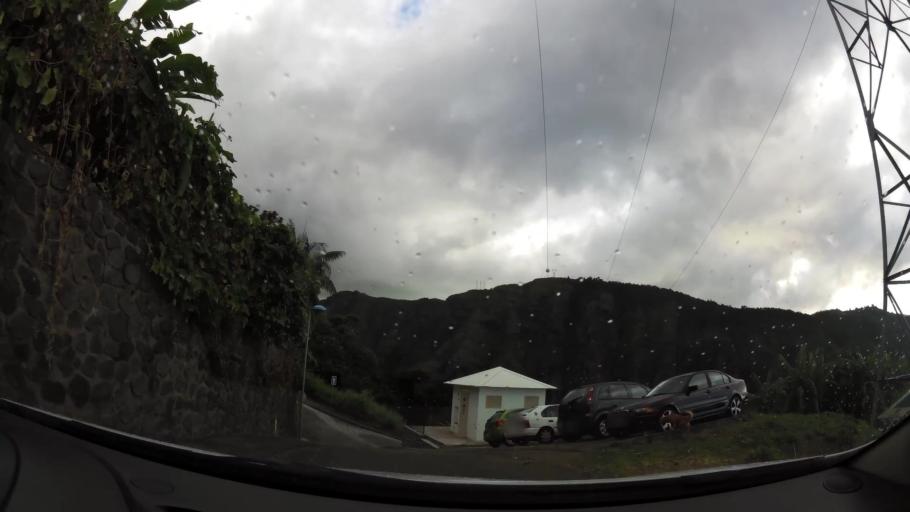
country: RE
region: Reunion
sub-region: Reunion
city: Saint-Denis
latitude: -20.9051
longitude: 55.4413
